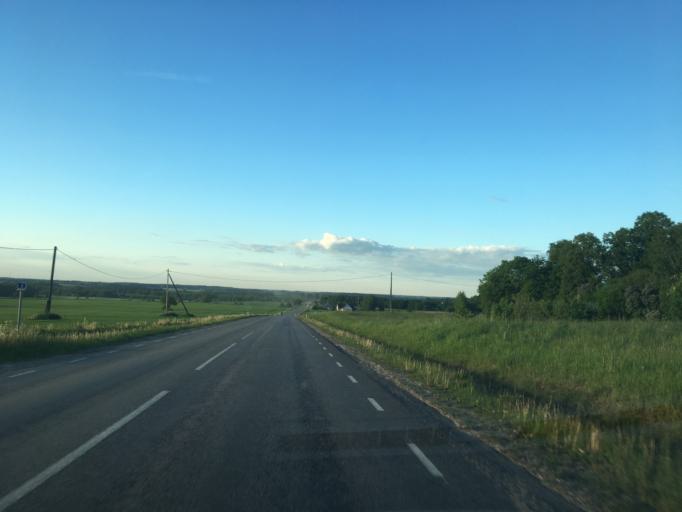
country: EE
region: Tartu
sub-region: Noo vald
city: Noo
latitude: 58.2291
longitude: 26.6421
